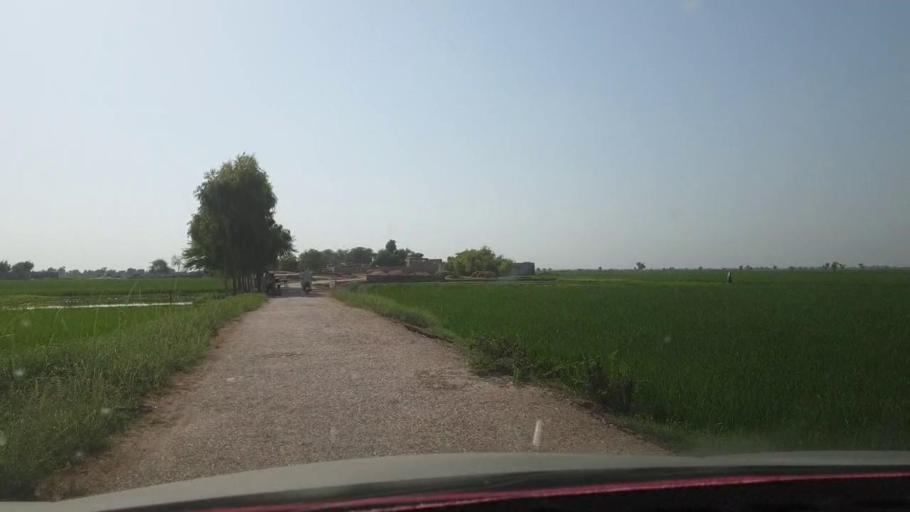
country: PK
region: Sindh
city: Nasirabad
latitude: 27.3846
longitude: 67.8746
